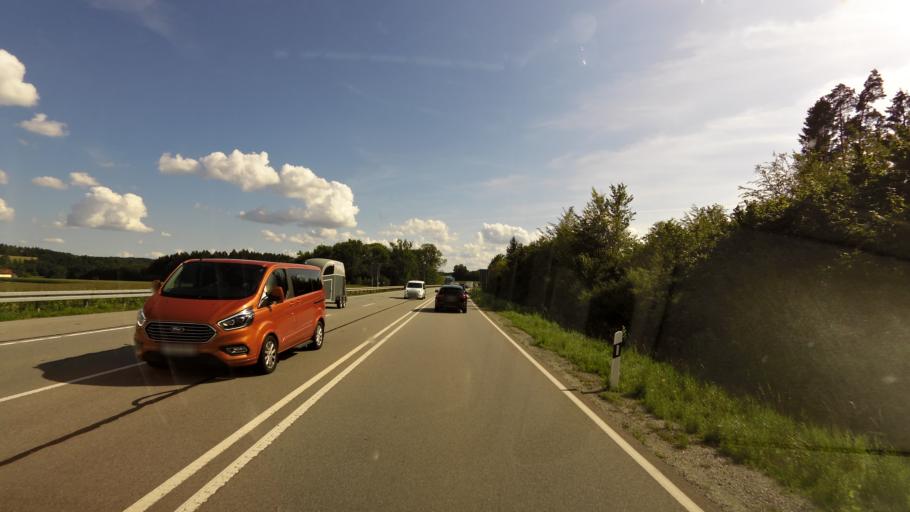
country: DE
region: Bavaria
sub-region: Lower Bavaria
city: Ascha
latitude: 48.9870
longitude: 12.6313
